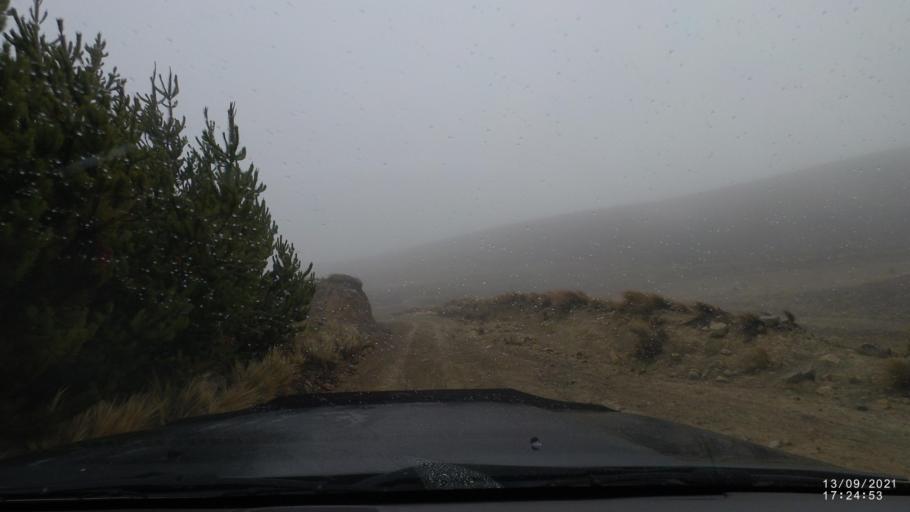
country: BO
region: Cochabamba
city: Colomi
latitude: -17.3569
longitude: -65.7790
